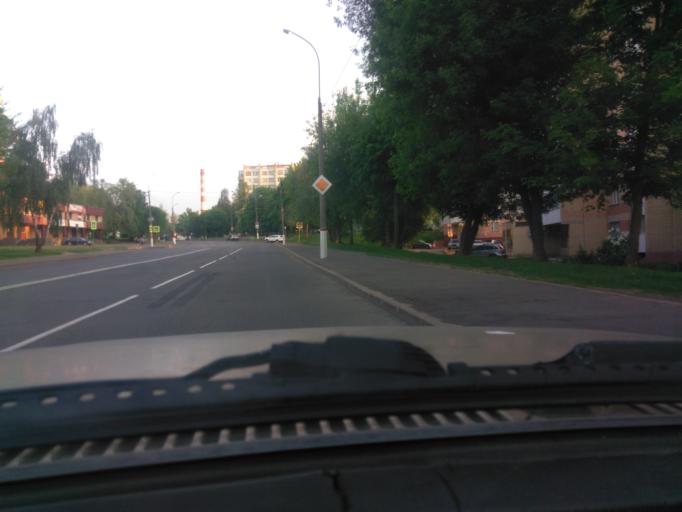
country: BY
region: Mogilev
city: Mahilyow
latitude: 53.9216
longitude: 30.3115
